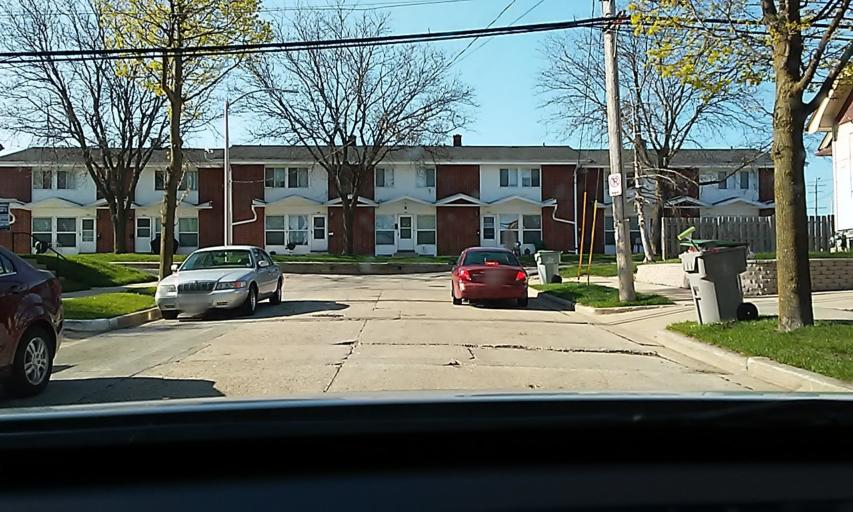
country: US
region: Wisconsin
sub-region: Milwaukee County
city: West Allis
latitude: 43.0269
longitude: -88.0195
